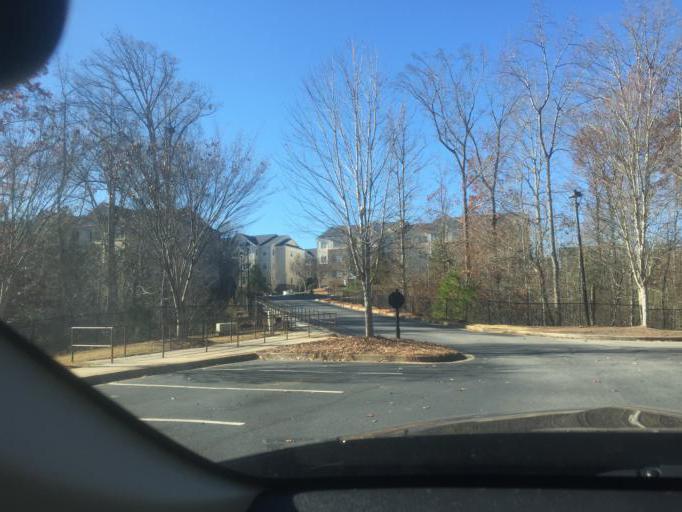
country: US
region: Georgia
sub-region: Fulton County
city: Fairburn
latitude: 33.6125
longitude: -84.6062
